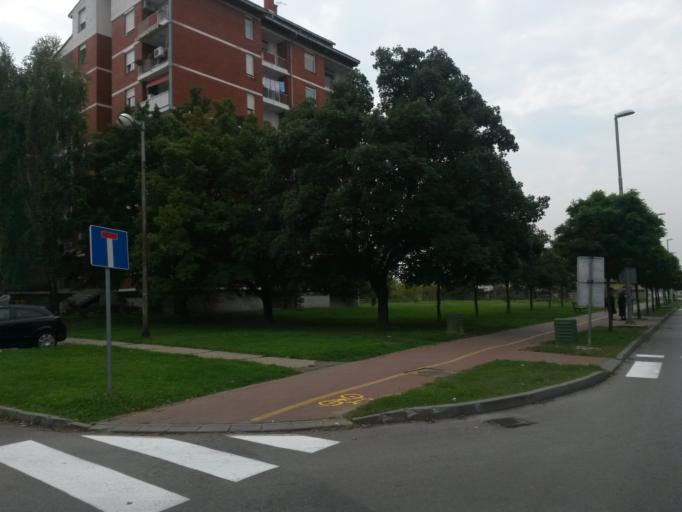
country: HR
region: Osjecko-Baranjska
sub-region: Grad Osijek
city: Osijek
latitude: 45.5432
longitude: 18.7134
